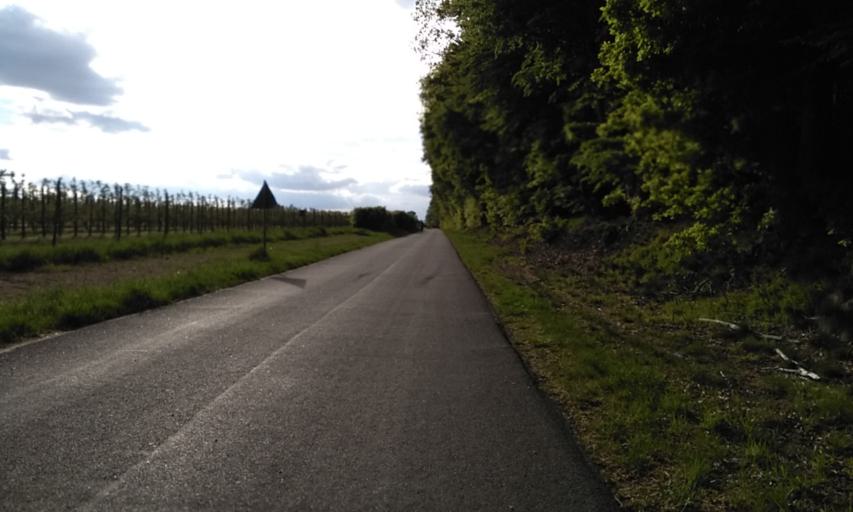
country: DE
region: Lower Saxony
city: Nottensdorf
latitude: 53.4801
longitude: 9.6121
